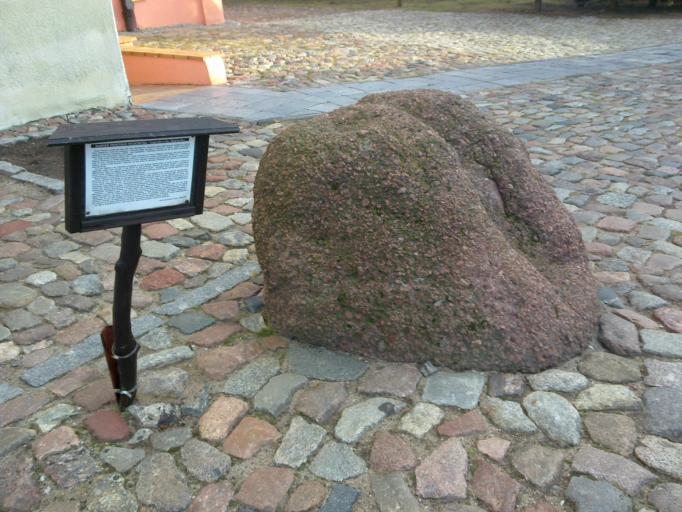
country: PL
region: Kujawsko-Pomorskie
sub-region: Powiat mogilenski
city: Strzelno
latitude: 52.6298
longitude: 18.1788
